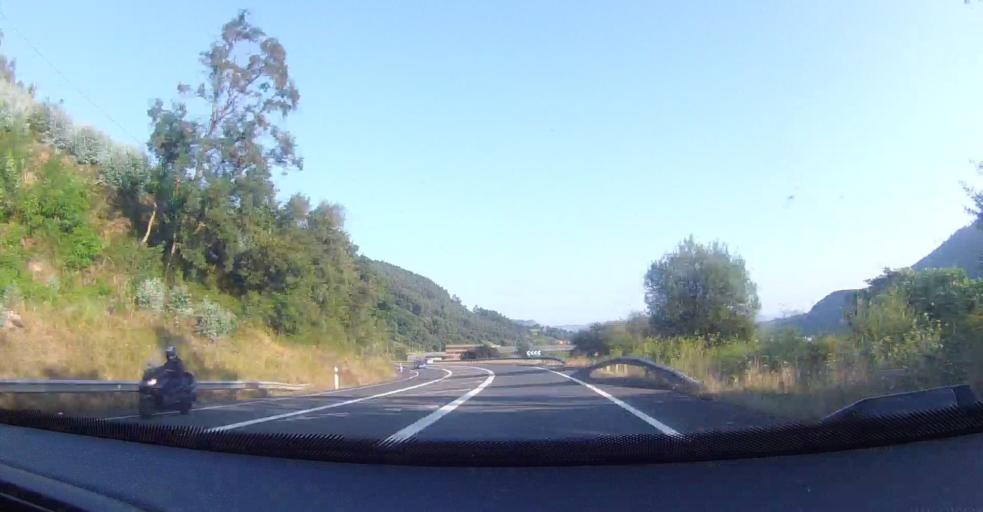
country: ES
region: Cantabria
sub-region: Provincia de Cantabria
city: Limpias
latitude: 43.3785
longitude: -3.4330
